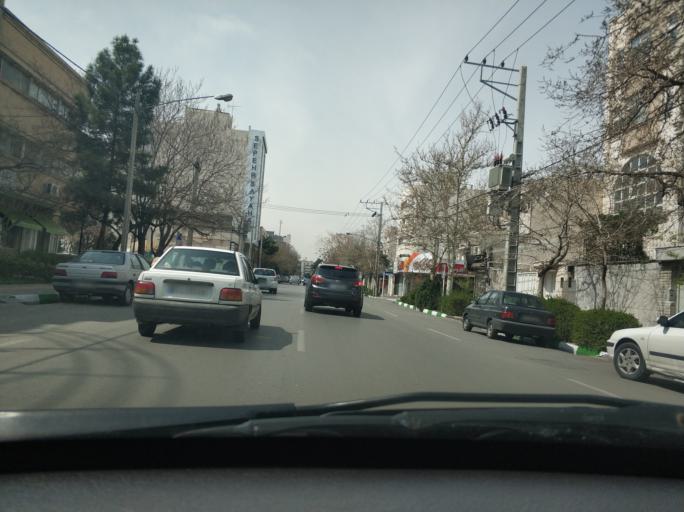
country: IR
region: Razavi Khorasan
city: Mashhad
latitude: 36.3050
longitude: 59.5683
